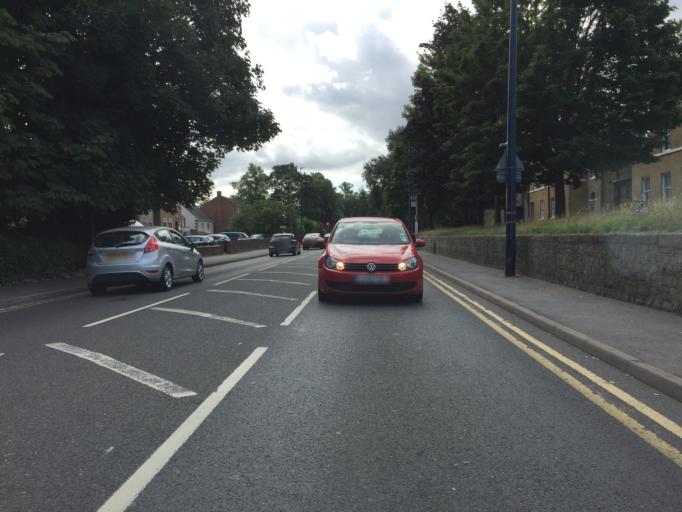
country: GB
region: England
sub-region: Kent
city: Maidstone
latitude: 51.2773
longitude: 0.5081
